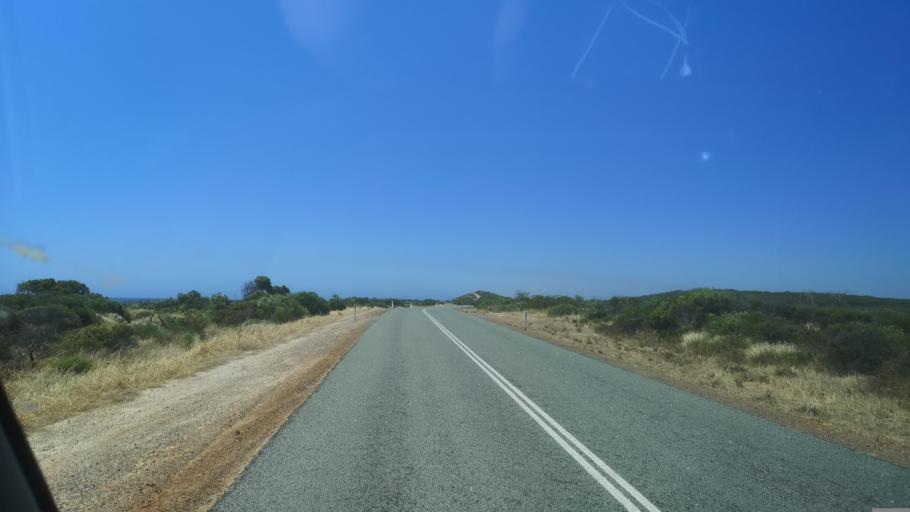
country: AU
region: Western Australia
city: Port Denison
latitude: -29.6707
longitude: 114.9609
